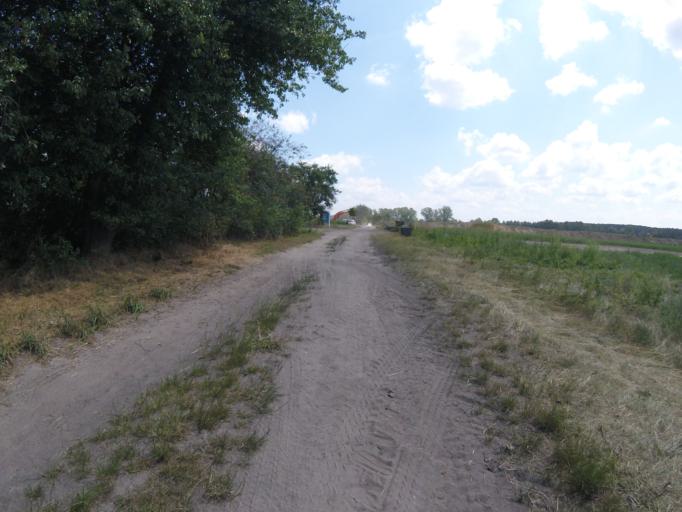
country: DE
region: Brandenburg
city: Bestensee
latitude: 52.2619
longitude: 13.7181
